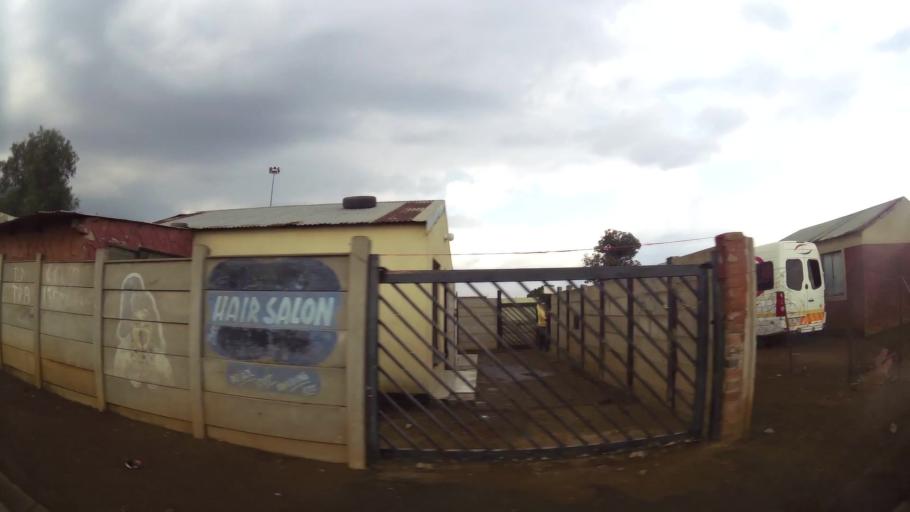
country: ZA
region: Gauteng
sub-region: Ekurhuleni Metropolitan Municipality
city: Germiston
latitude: -26.3639
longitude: 28.1248
